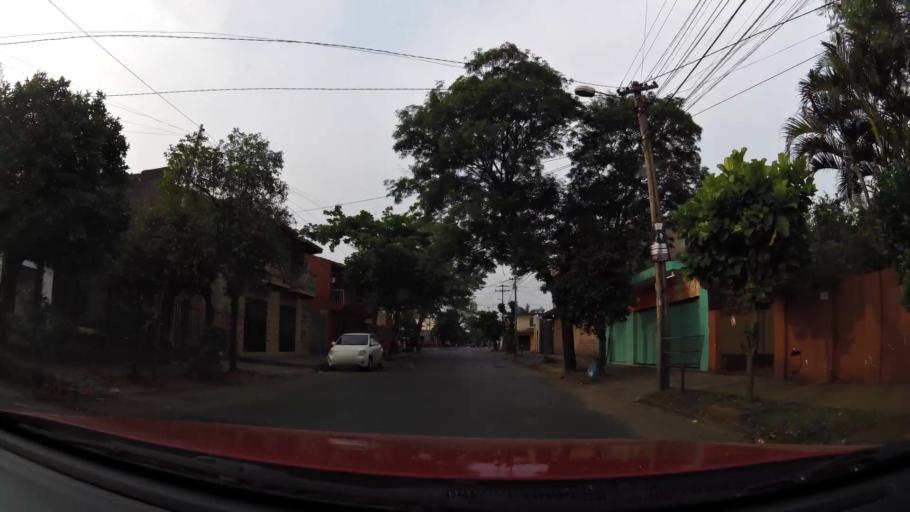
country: PY
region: Central
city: Lambare
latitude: -25.3209
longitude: -57.5734
